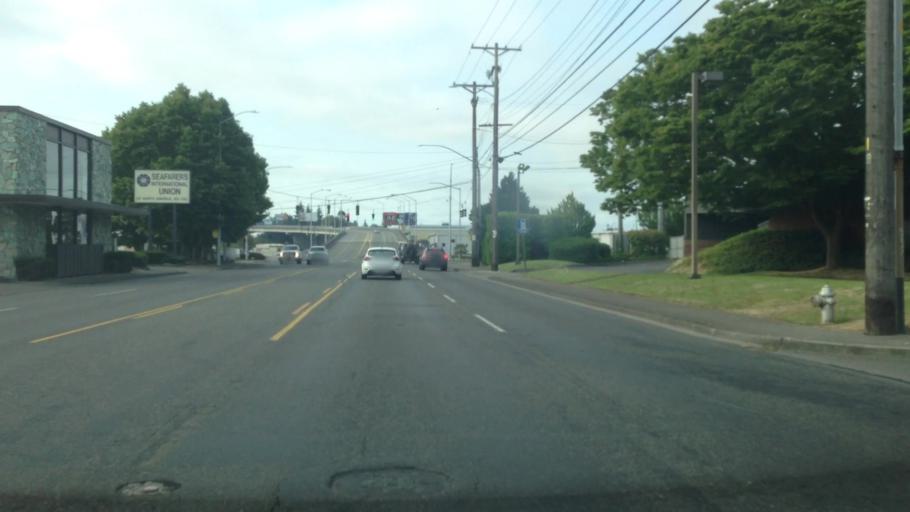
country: US
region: Washington
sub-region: Pierce County
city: Fircrest
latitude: 47.2293
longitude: -122.4837
